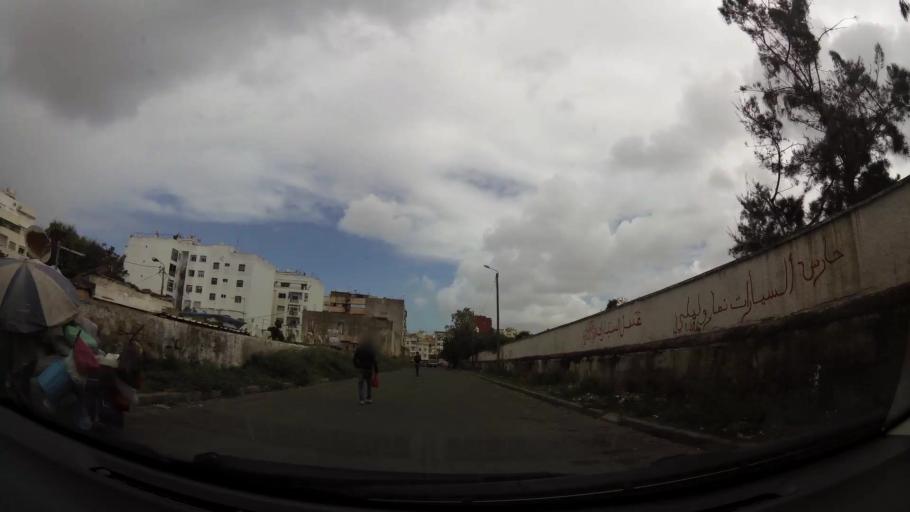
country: MA
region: Grand Casablanca
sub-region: Casablanca
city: Casablanca
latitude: 33.5962
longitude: -7.6450
